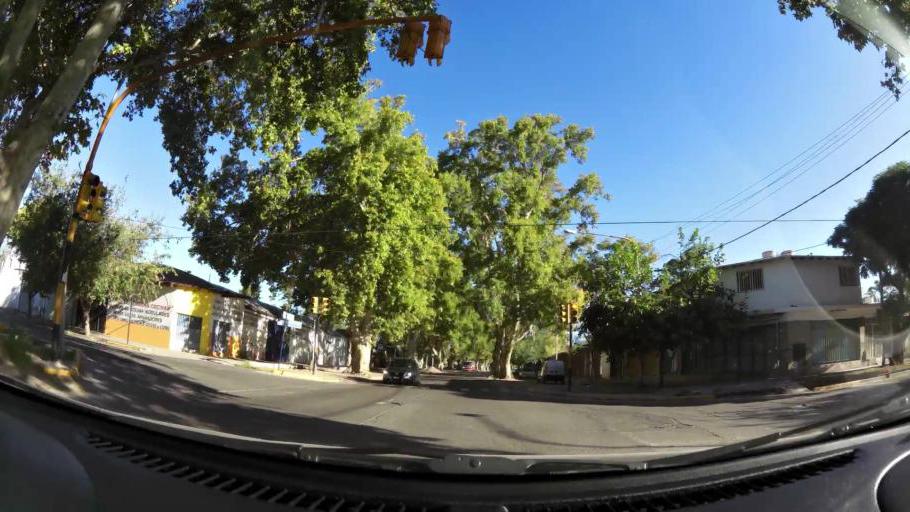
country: AR
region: Mendoza
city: Las Heras
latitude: -32.8520
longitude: -68.8269
